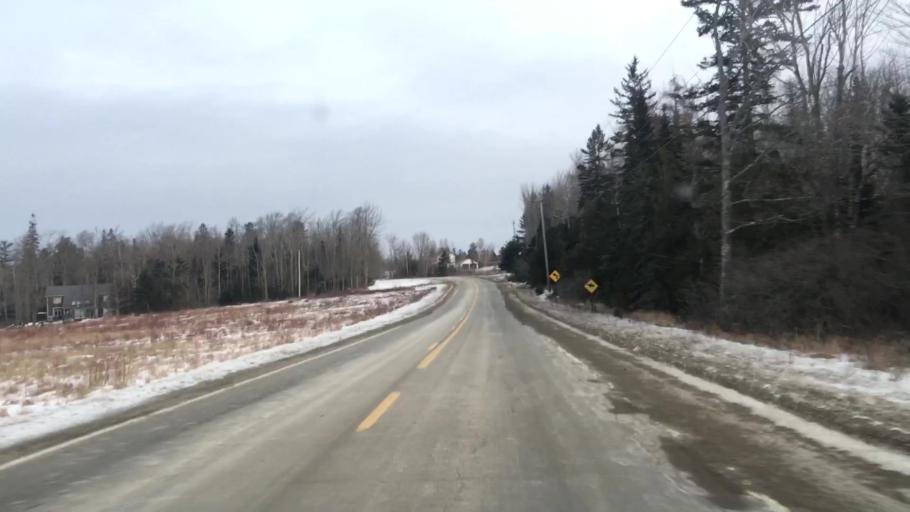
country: US
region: Maine
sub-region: Hancock County
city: Franklin
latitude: 44.7221
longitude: -68.3348
